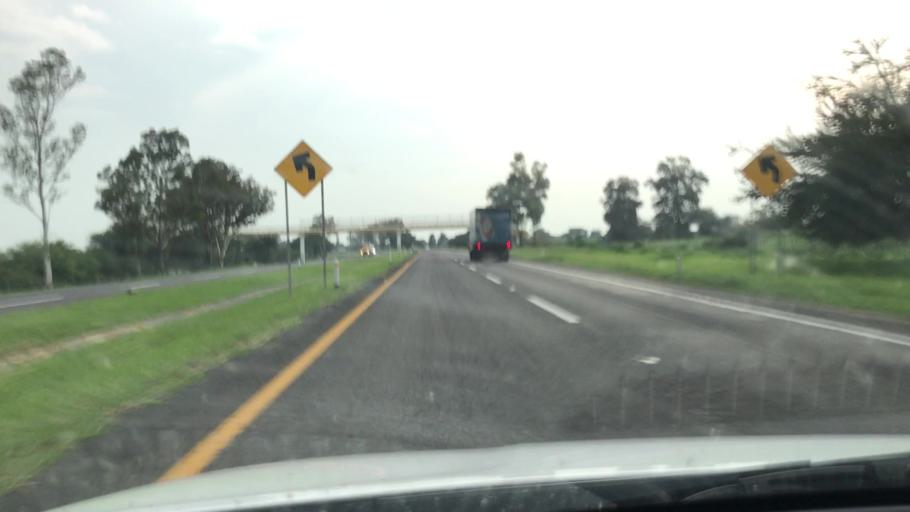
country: MX
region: Jalisco
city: La Barca
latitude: 20.3319
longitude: -102.5881
